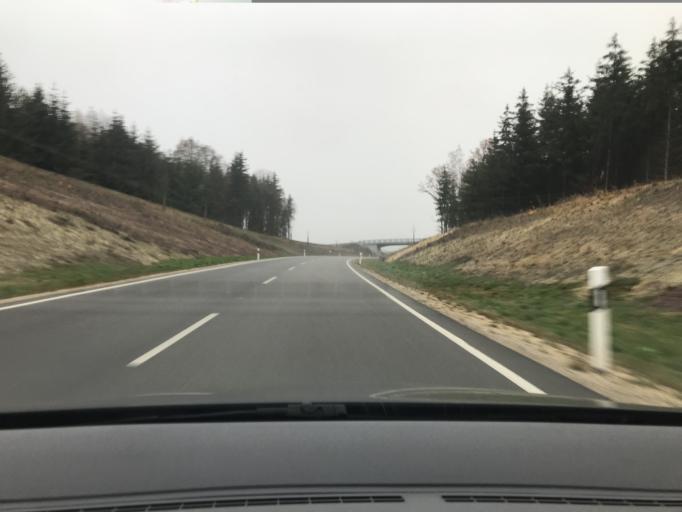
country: DE
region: Bavaria
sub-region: Swabia
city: Fremdingen
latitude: 48.9692
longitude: 10.4489
